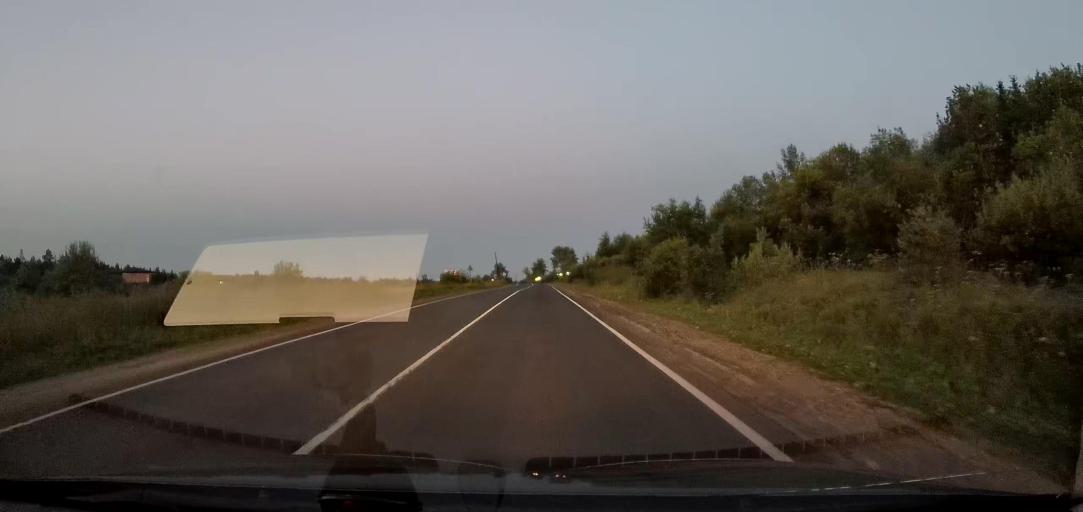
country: RU
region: Arkhangelskaya
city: Uyemskiy
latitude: 64.4487
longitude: 40.9452
